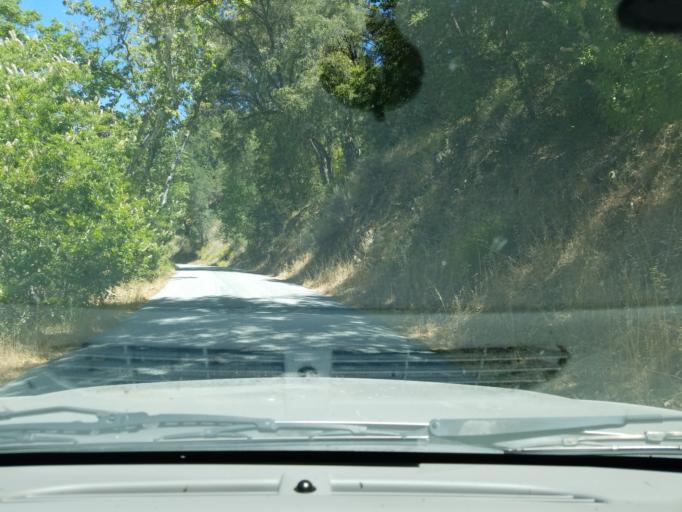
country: US
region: California
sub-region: Monterey County
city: Gonzales
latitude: 36.3691
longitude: -121.5599
